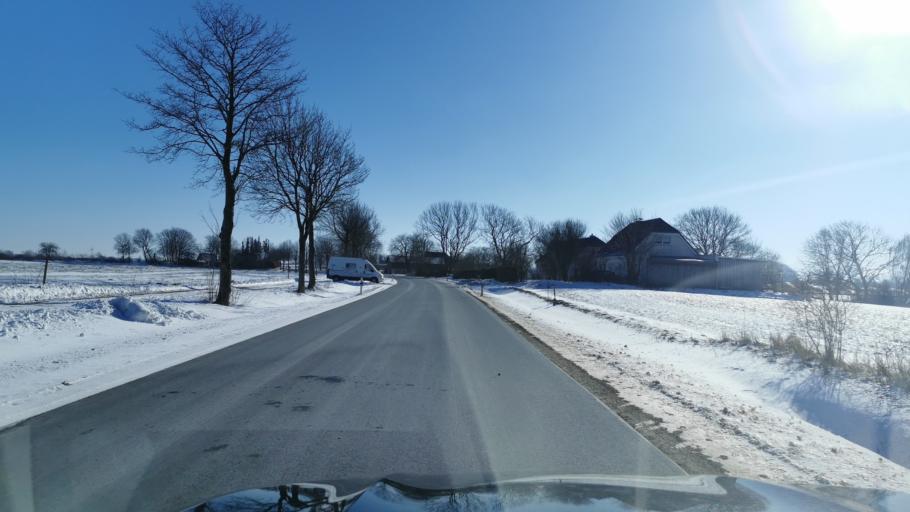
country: DE
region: Schleswig-Holstein
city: Langballig
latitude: 54.7910
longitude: 9.6404
